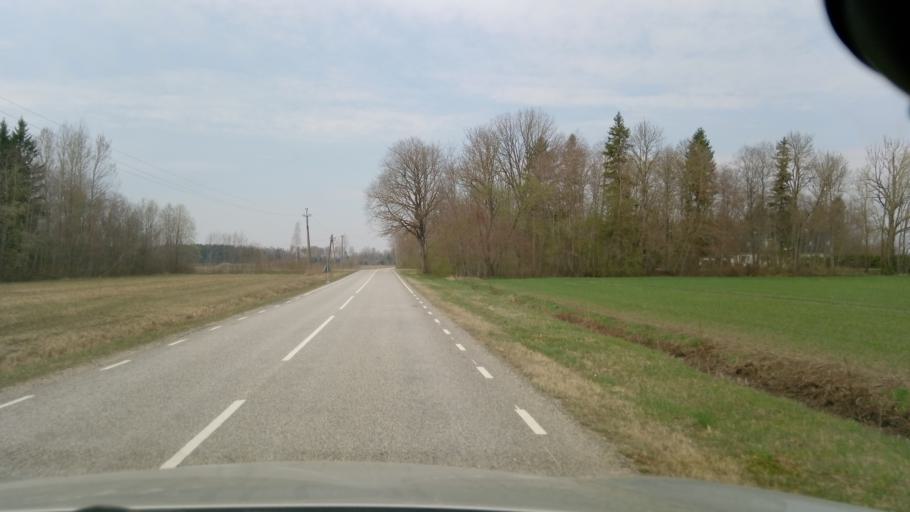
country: EE
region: Jaervamaa
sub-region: Tueri vald
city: Tueri
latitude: 58.8034
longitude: 25.4725
